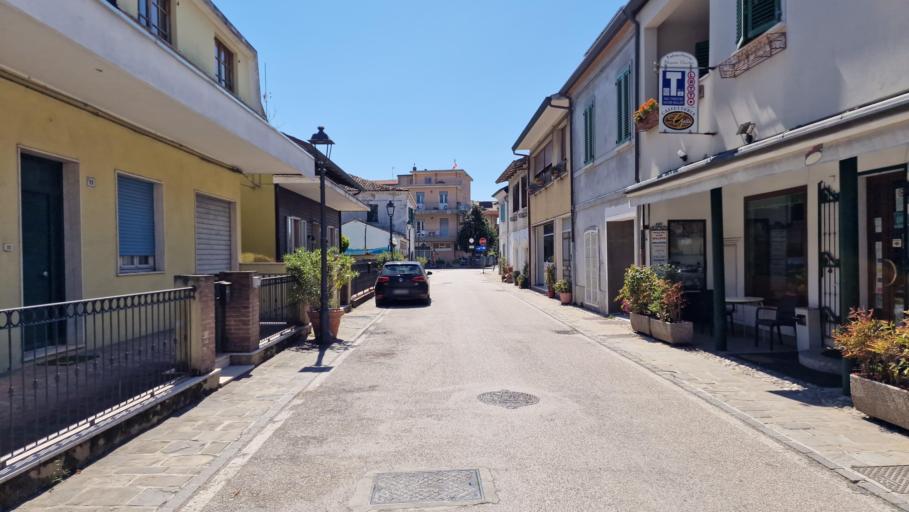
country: IT
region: Emilia-Romagna
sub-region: Provincia di Rimini
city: Bellaria-Igea Marina
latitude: 44.1452
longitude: 12.4593
